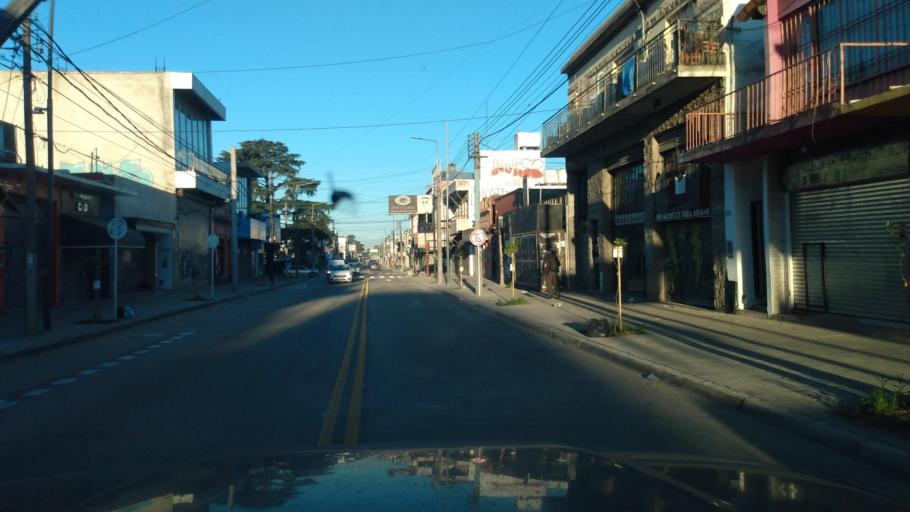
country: AR
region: Buenos Aires
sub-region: Partido de Merlo
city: Merlo
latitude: -34.6500
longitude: -58.7866
